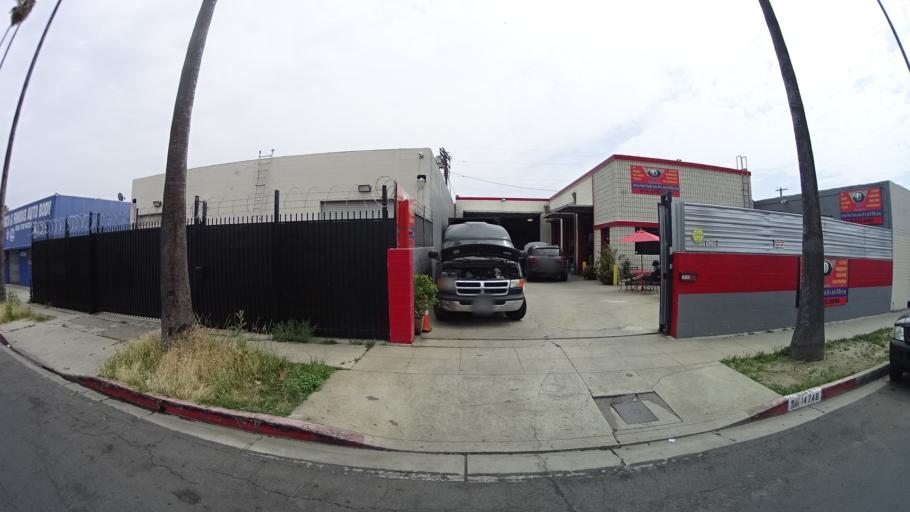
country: US
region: California
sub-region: Los Angeles County
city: Van Nuys
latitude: 34.1817
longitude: -118.4548
